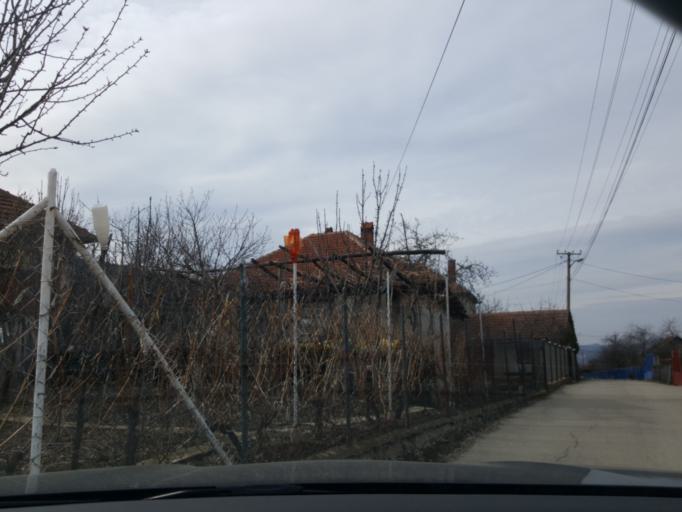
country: RS
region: Central Serbia
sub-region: Pirotski Okrug
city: Dimitrovgrad
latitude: 43.0083
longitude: 22.7513
